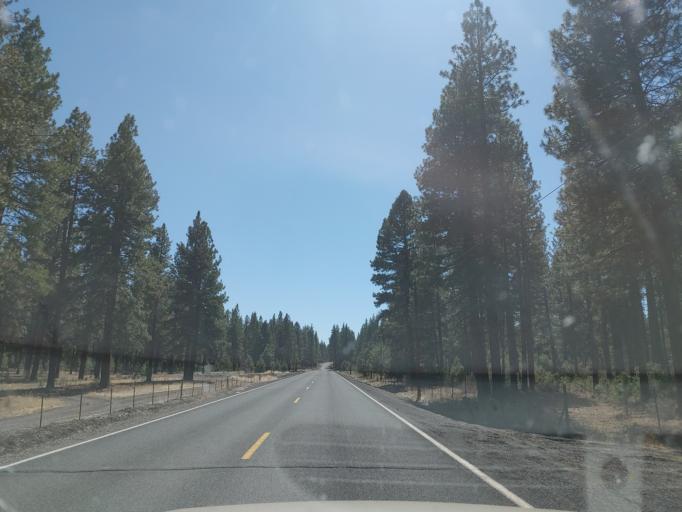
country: US
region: Oregon
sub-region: Klamath County
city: Klamath Falls
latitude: 42.5550
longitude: -121.8948
